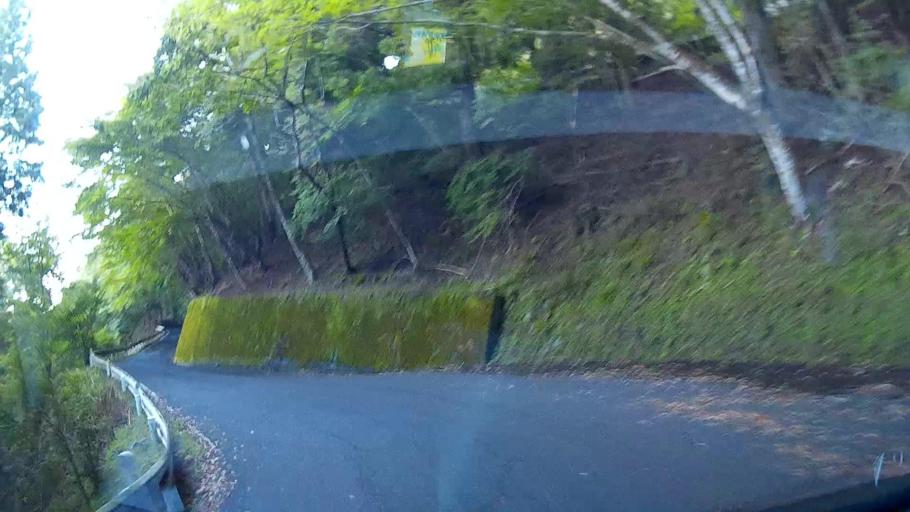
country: JP
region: Shizuoka
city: Shizuoka-shi
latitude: 35.1722
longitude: 138.2582
